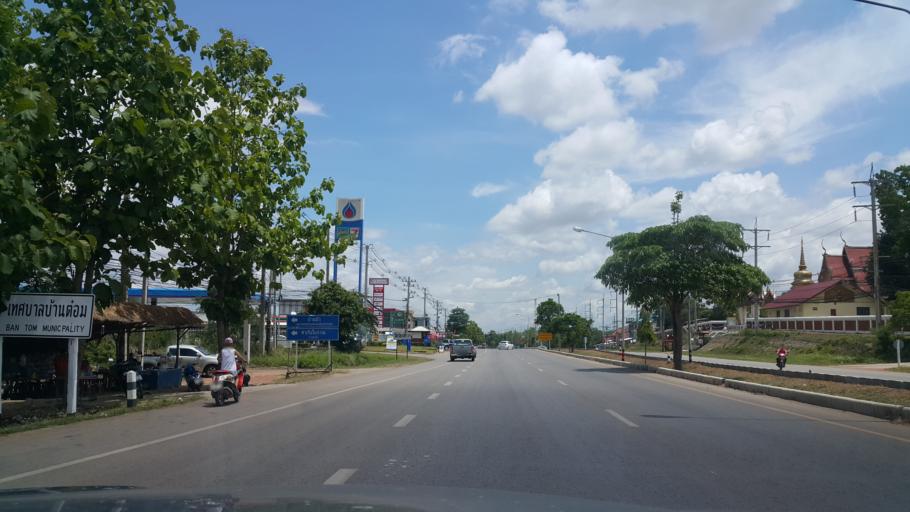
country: TH
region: Phayao
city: Phayao
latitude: 19.2049
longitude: 99.8718
